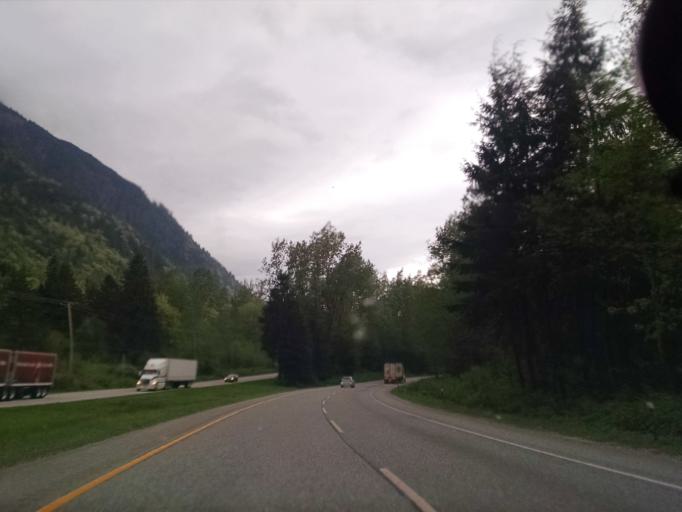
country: CA
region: British Columbia
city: Agassiz
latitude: 49.2173
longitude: -121.6926
